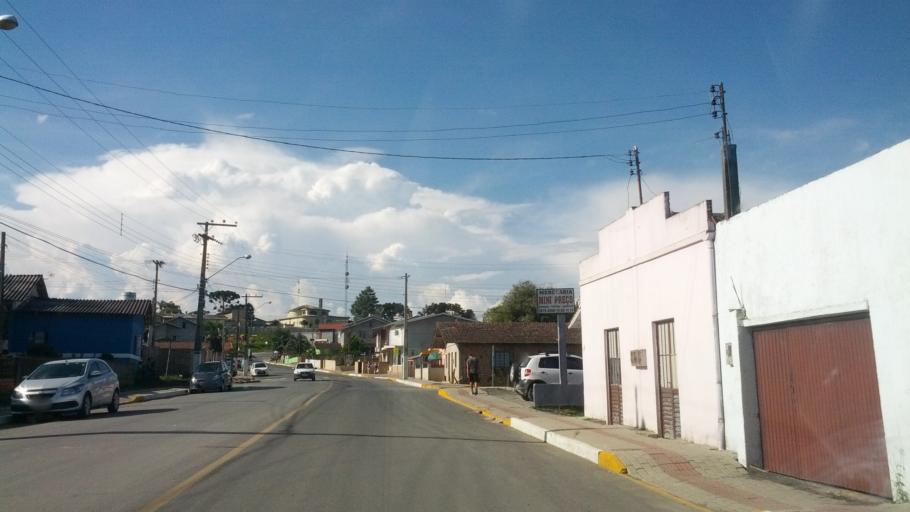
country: BR
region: Santa Catarina
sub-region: Otacilio Costa
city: Otacilio Costa
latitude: -27.4890
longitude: -50.1219
